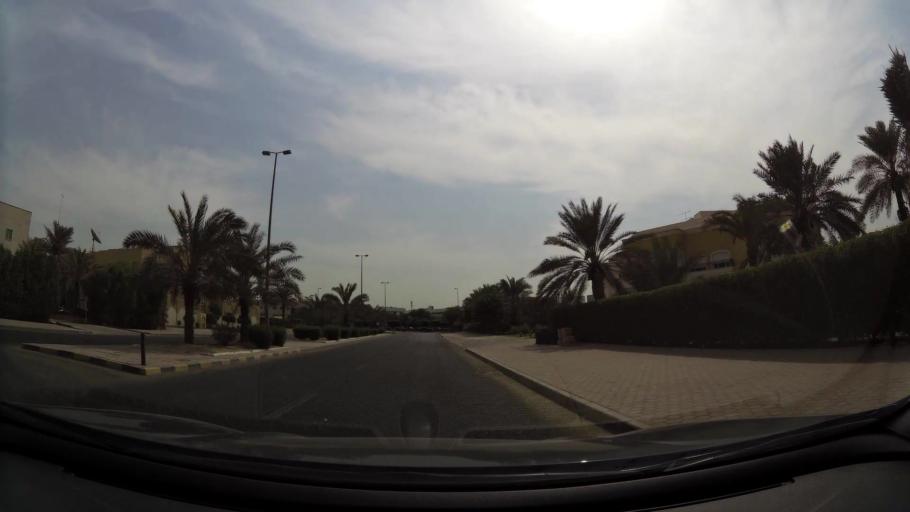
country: KW
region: Al Asimah
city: Ash Shamiyah
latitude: 29.3347
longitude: 47.9817
